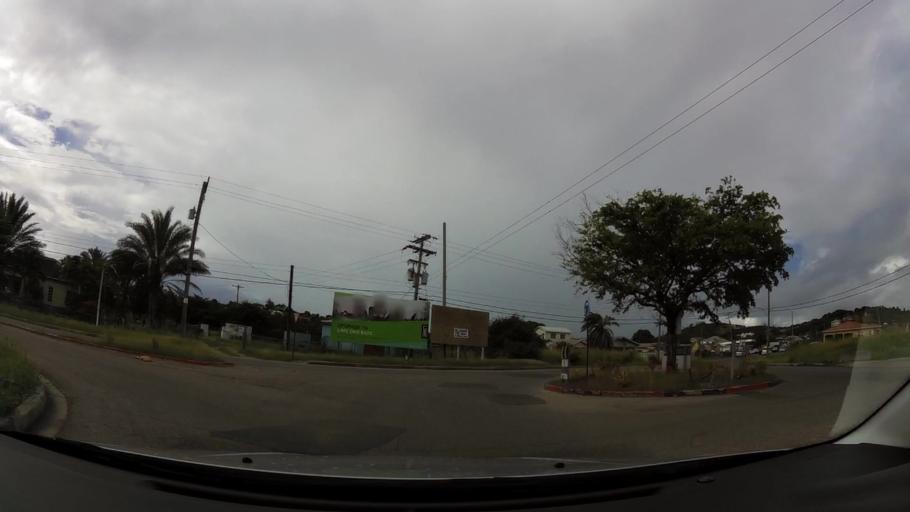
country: AG
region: Saint John
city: Potters Village
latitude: 17.0918
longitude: -61.8174
